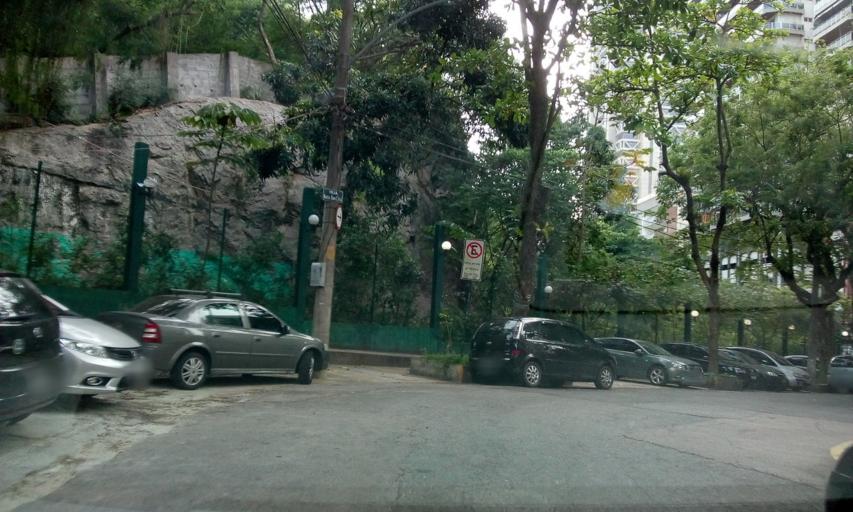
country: BR
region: Rio de Janeiro
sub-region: Rio De Janeiro
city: Rio de Janeiro
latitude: -22.9556
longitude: -43.1737
